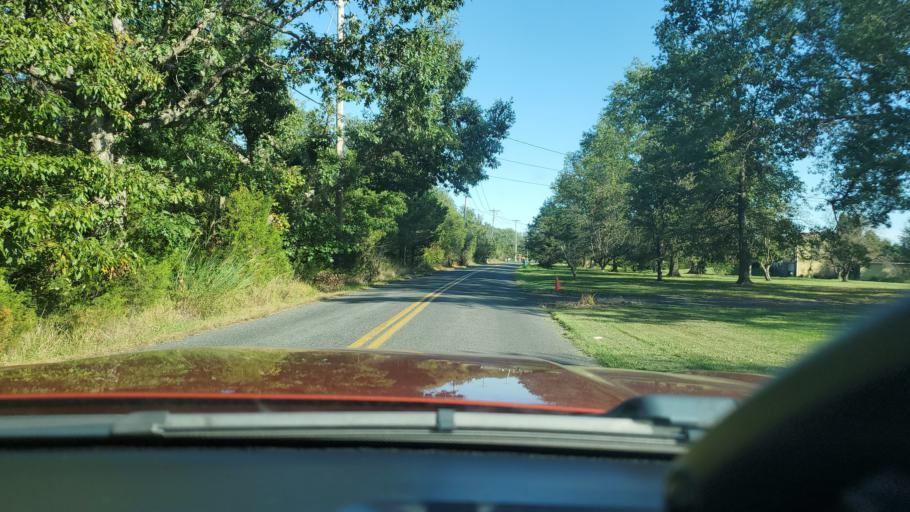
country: US
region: Pennsylvania
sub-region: Montgomery County
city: Woxall
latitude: 40.3056
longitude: -75.5081
